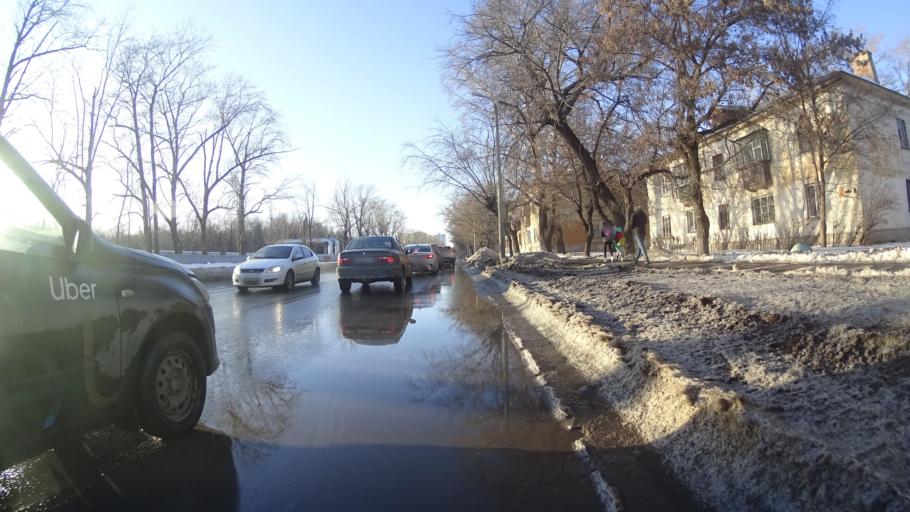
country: RU
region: Chelyabinsk
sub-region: Gorod Chelyabinsk
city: Chelyabinsk
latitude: 55.1326
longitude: 61.4617
